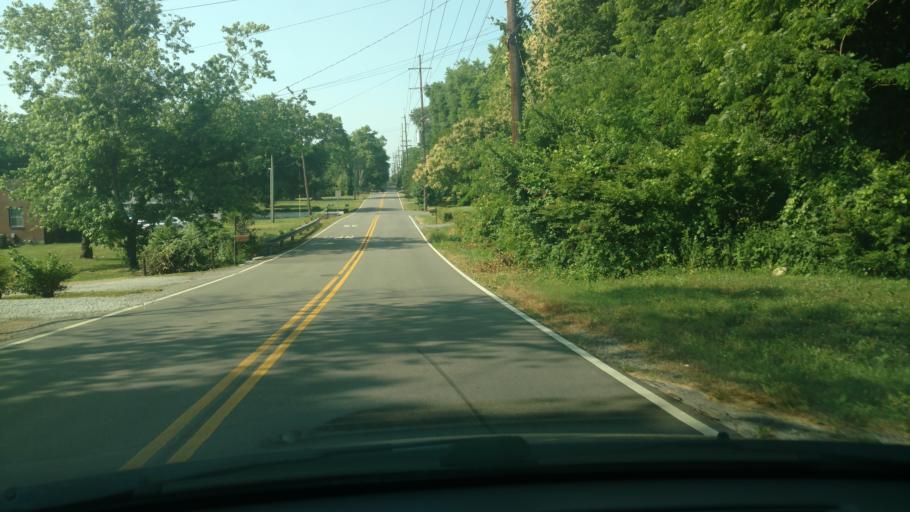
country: US
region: Tennessee
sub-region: Davidson County
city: Nashville
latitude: 36.2237
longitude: -86.7349
